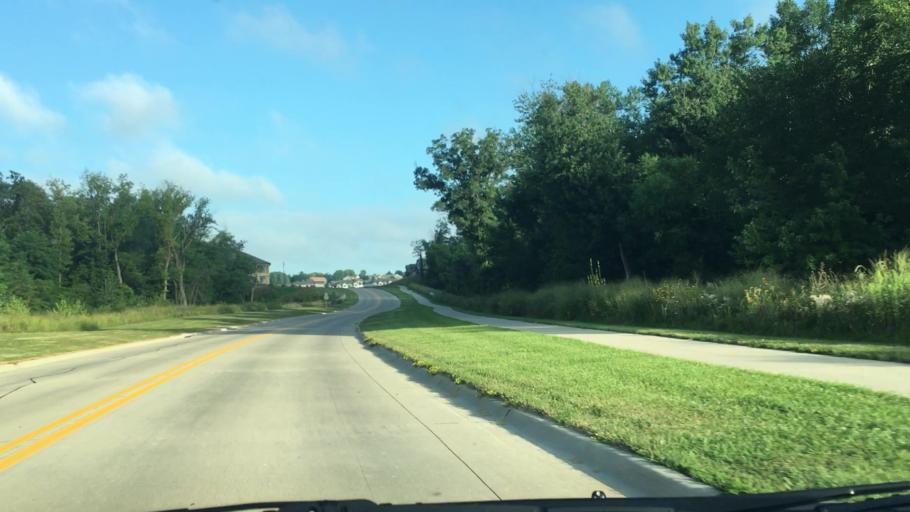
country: US
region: Iowa
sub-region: Johnson County
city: Coralville
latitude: 41.6998
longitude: -91.5498
